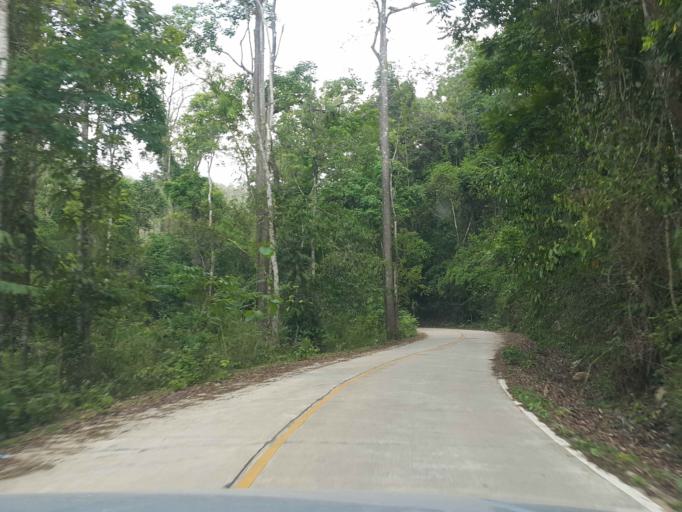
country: TH
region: Chiang Mai
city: Wiang Haeng
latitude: 19.3787
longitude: 98.7467
